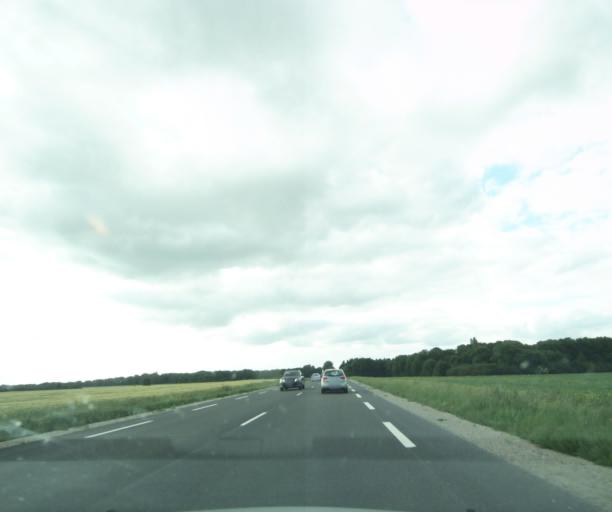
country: FR
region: Centre
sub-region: Departement d'Eure-et-Loir
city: Sours
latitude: 48.3984
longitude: 1.5579
